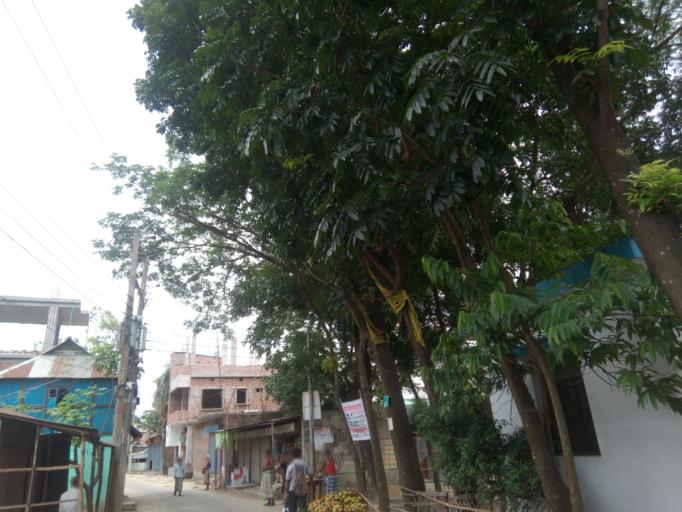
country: BD
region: Dhaka
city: Paltan
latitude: 23.7359
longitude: 90.4877
